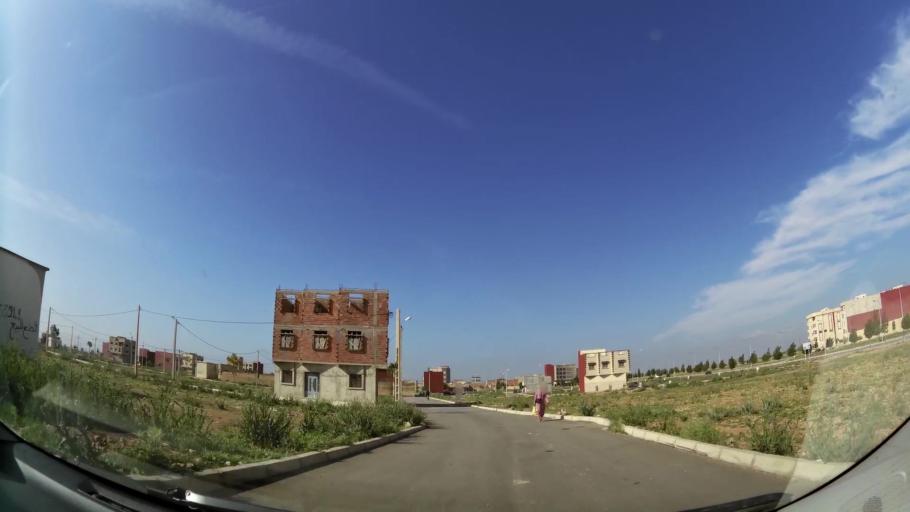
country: MA
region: Oriental
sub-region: Oujda-Angad
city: Oujda
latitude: 34.7149
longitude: -1.8857
